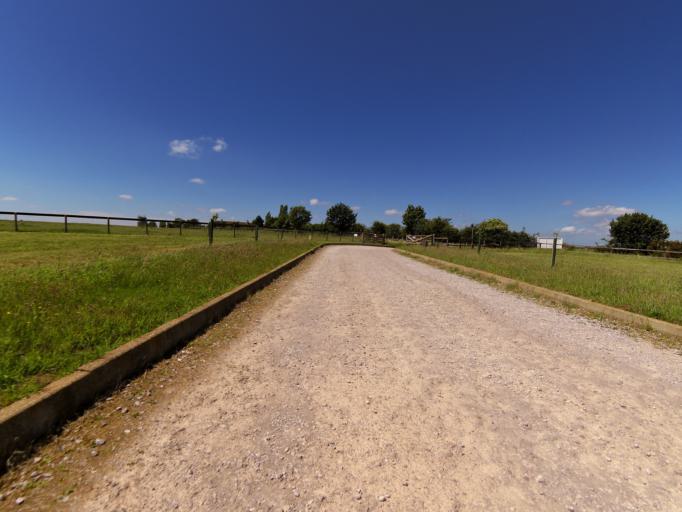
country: GB
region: England
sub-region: Suffolk
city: Wickham Market
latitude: 52.0576
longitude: 1.4454
